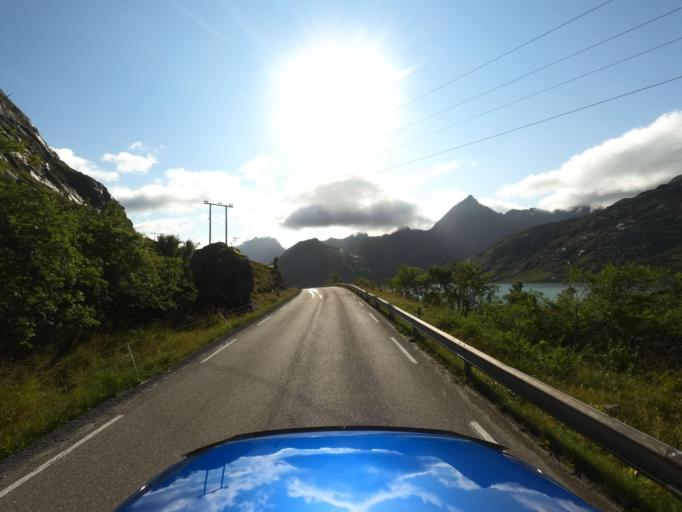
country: NO
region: Nordland
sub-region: Flakstad
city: Ramberg
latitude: 68.0985
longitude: 13.3397
